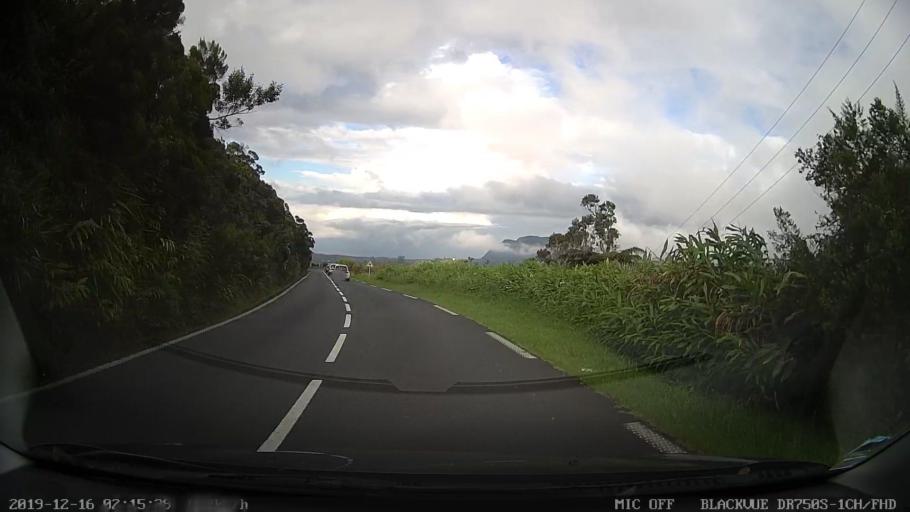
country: RE
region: Reunion
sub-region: Reunion
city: Cilaos
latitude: -21.1571
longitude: 55.5985
